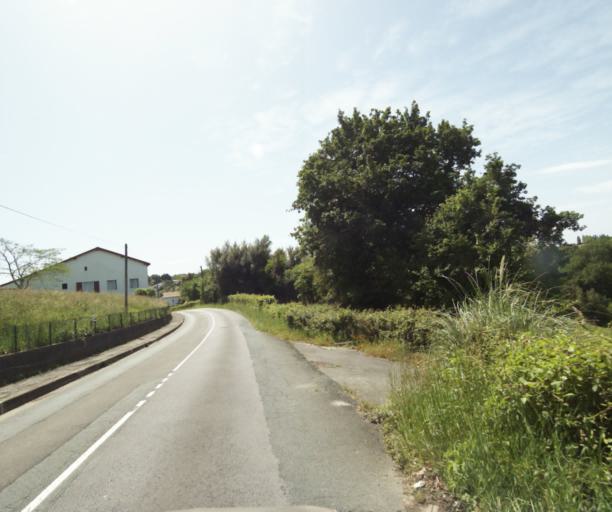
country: FR
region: Aquitaine
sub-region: Departement des Pyrenees-Atlantiques
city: Mouguerre
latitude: 43.4642
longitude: -1.4426
